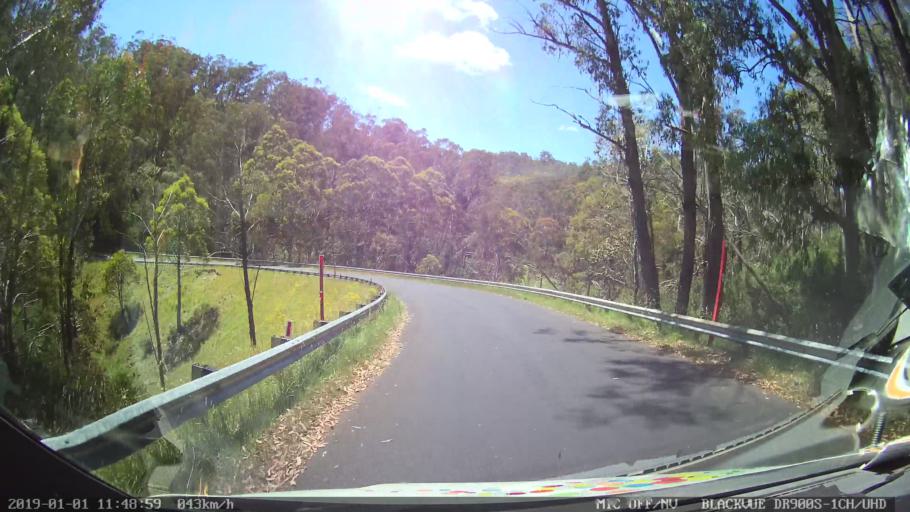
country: AU
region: New South Wales
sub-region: Snowy River
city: Jindabyne
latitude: -35.8959
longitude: 148.4129
